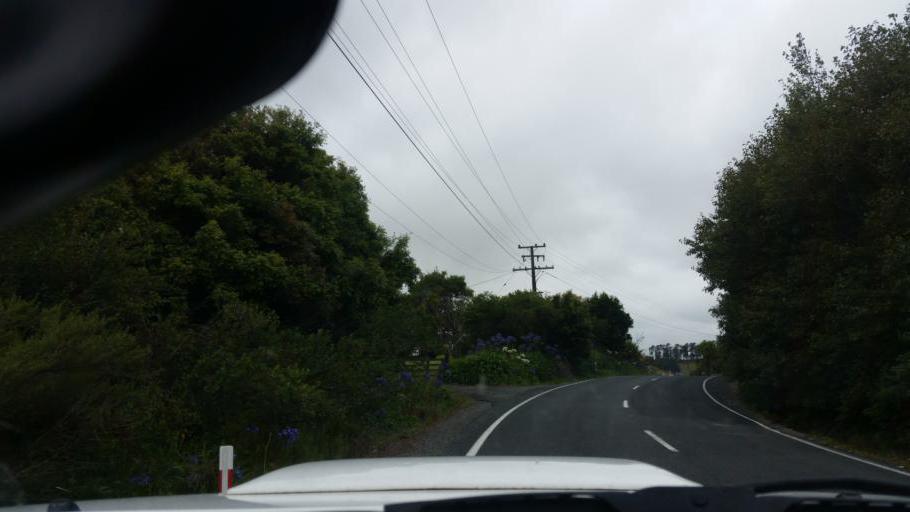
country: NZ
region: Auckland
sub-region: Auckland
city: Wellsford
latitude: -36.1471
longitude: 174.4766
